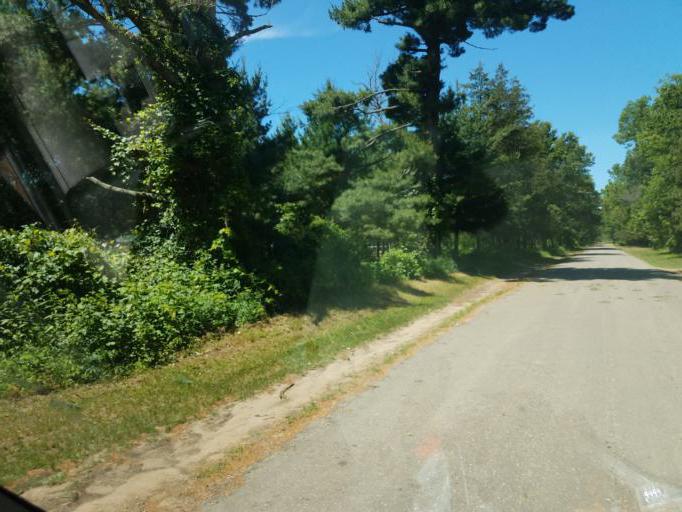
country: US
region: Wisconsin
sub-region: Adams County
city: Friendship
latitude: 44.0252
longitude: -89.9643
